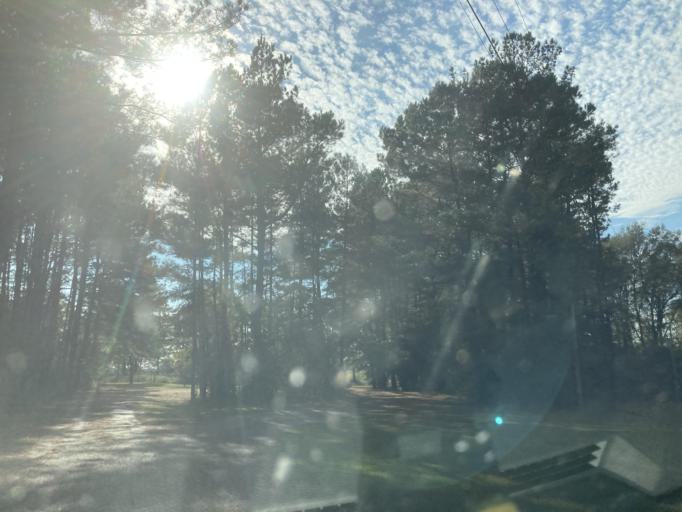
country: US
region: Mississippi
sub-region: Lamar County
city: Purvis
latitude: 31.2120
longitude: -89.3666
